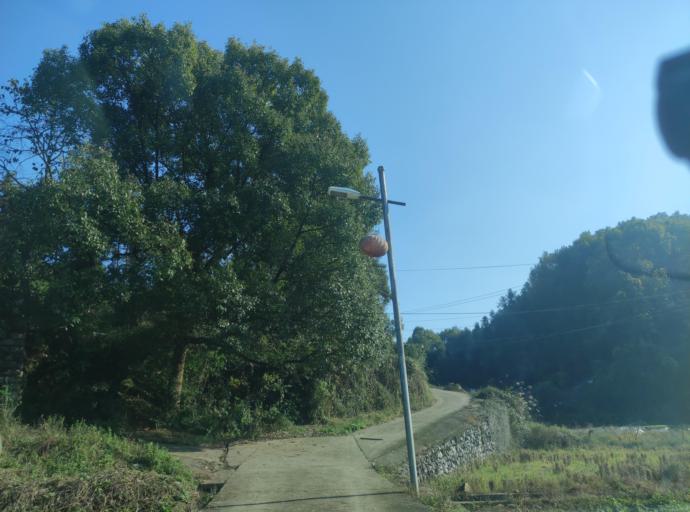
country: CN
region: Jiangxi Sheng
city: Xiangdong
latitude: 27.6547
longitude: 113.6642
